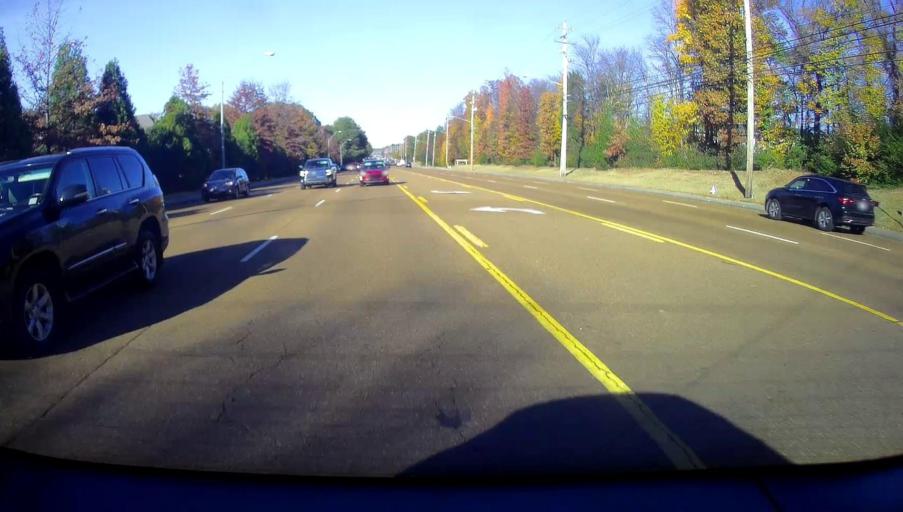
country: US
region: Tennessee
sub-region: Shelby County
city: Germantown
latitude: 35.1047
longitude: -89.8043
